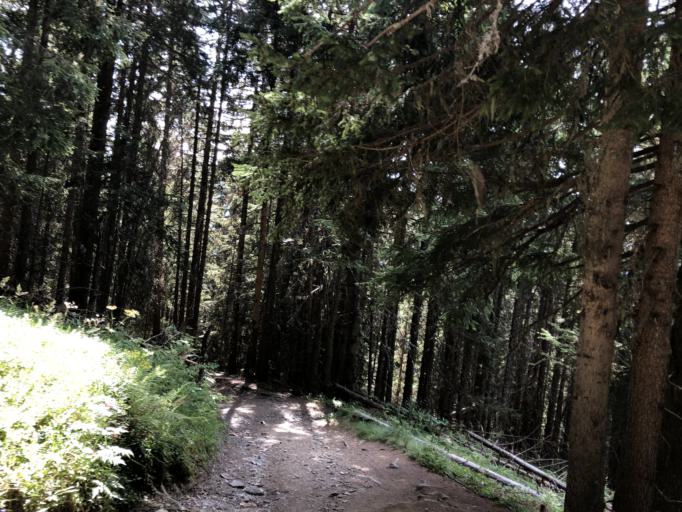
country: FR
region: Rhone-Alpes
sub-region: Departement de la Haute-Savoie
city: Megeve
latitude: 45.8243
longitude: 6.6585
